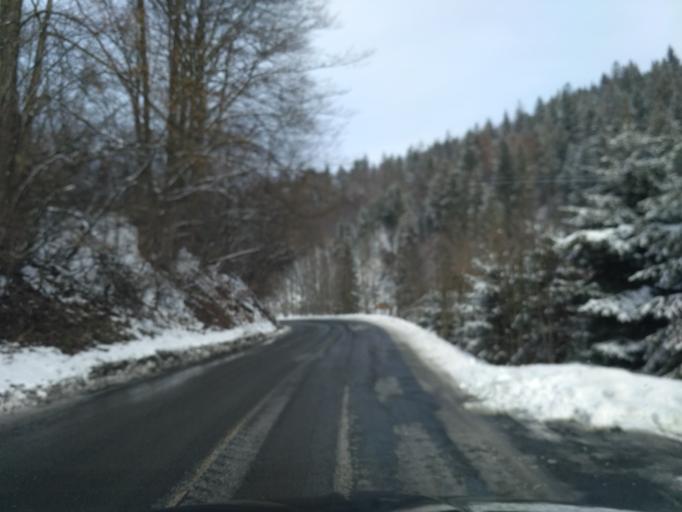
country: CZ
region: Zlin
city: Vidce
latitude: 49.4217
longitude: 18.0846
